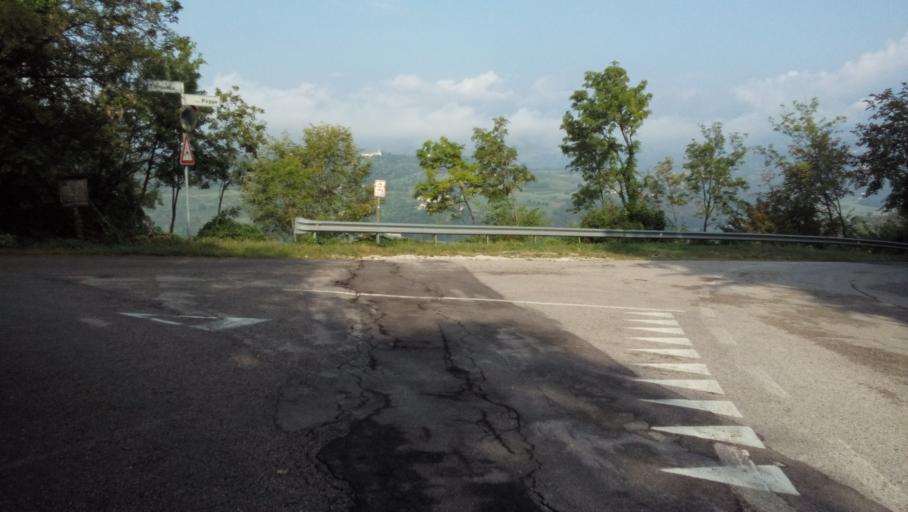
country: IT
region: Veneto
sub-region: Provincia di Vicenza
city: Monteviale
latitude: 45.5467
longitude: 11.4587
